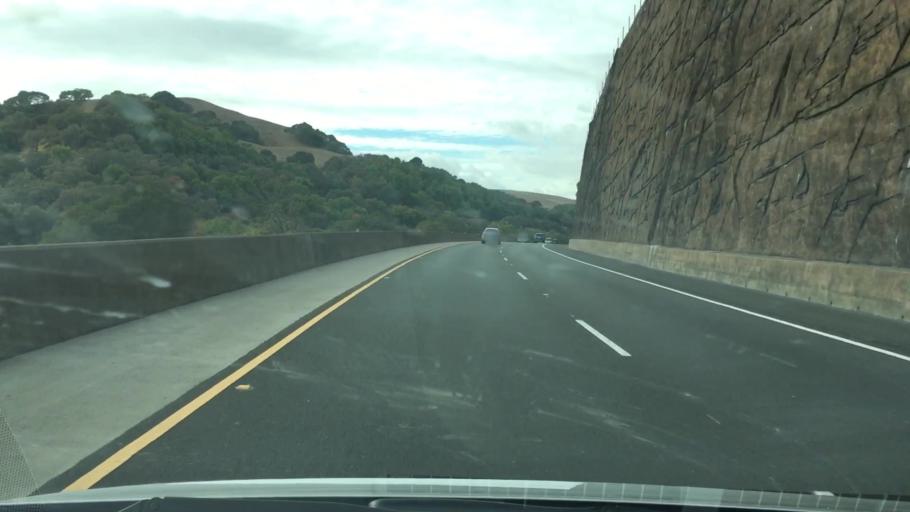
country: US
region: California
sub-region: Solano County
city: Green Valley
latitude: 38.2071
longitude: -122.1725
